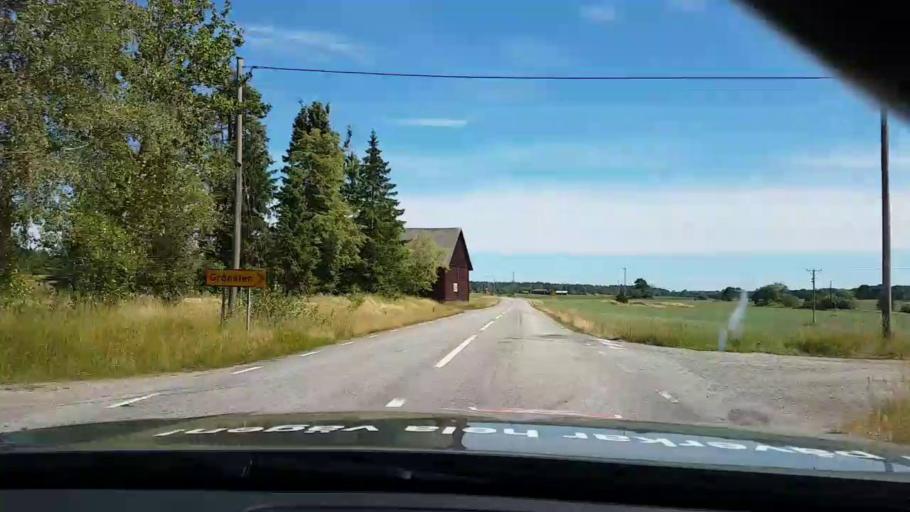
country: SE
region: Kalmar
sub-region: Vasterviks Kommun
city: Forserum
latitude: 57.9348
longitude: 16.5051
